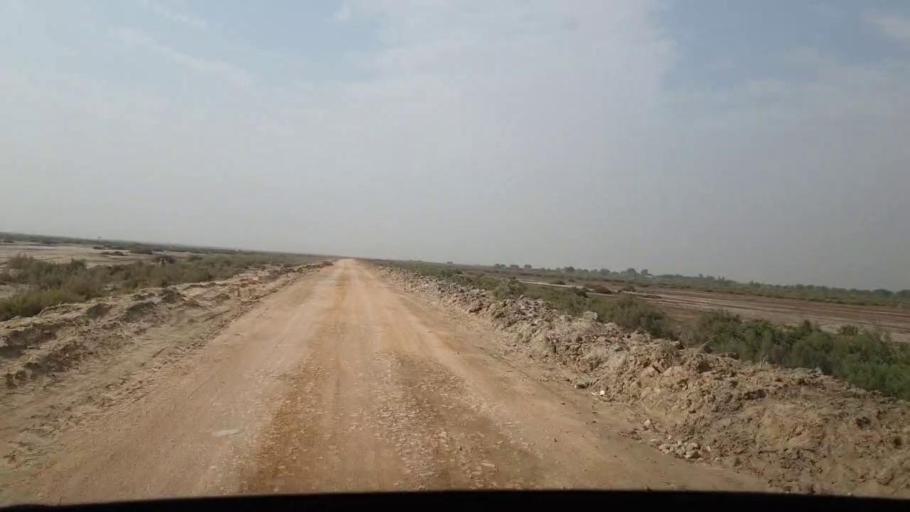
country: PK
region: Sindh
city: Chuhar Jamali
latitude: 24.3581
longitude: 67.9297
